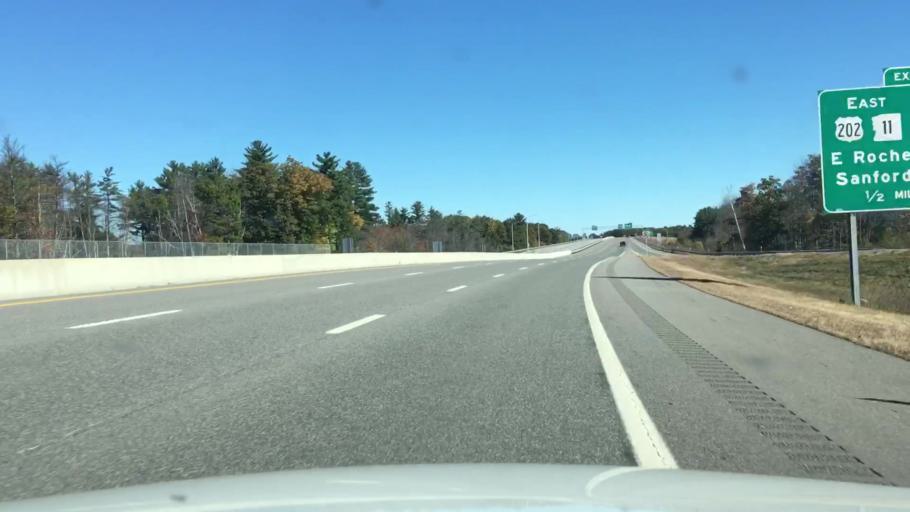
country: US
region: New Hampshire
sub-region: Strafford County
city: Rochester
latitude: 43.3198
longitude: -70.9944
